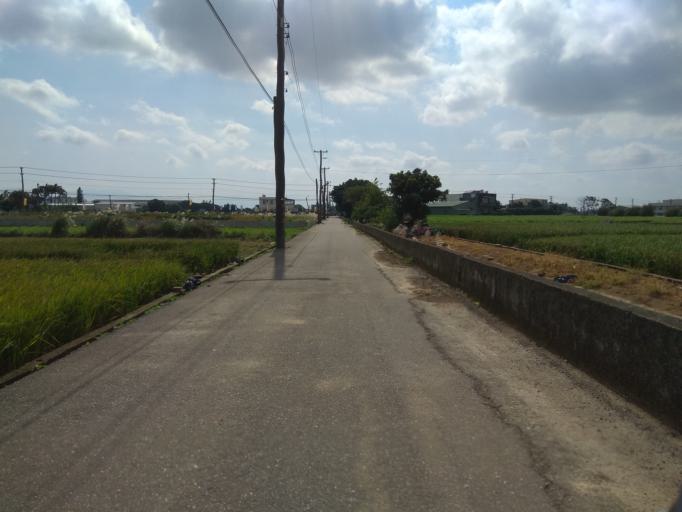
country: TW
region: Taiwan
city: Taoyuan City
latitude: 25.0742
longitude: 121.2489
